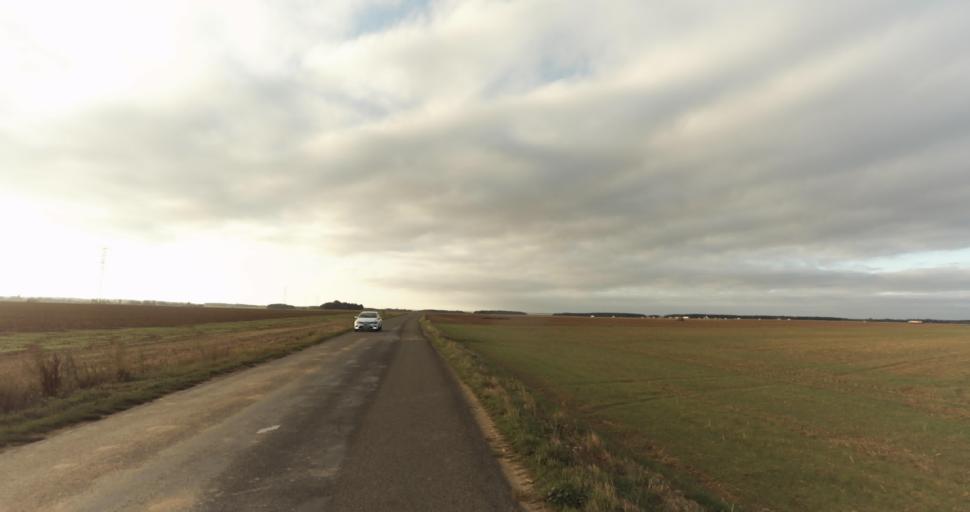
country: FR
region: Centre
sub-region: Departement d'Eure-et-Loir
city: Vernouillet
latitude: 48.7079
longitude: 1.3822
